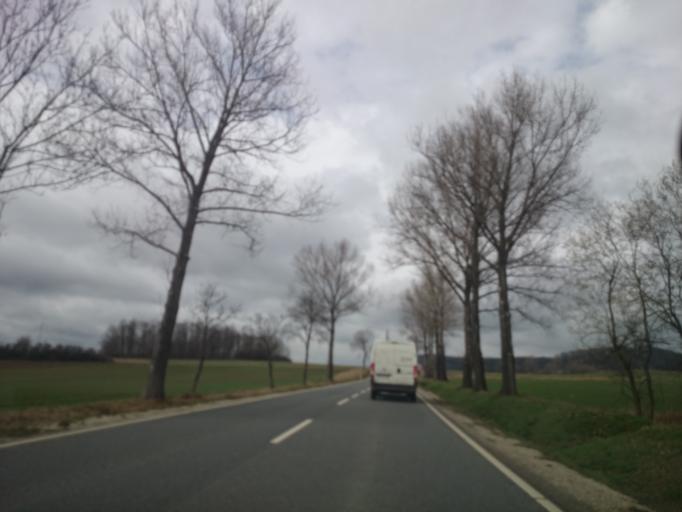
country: PL
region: Lower Silesian Voivodeship
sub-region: Powiat klodzki
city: Bystrzyca Klodzka
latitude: 50.3365
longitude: 16.6631
